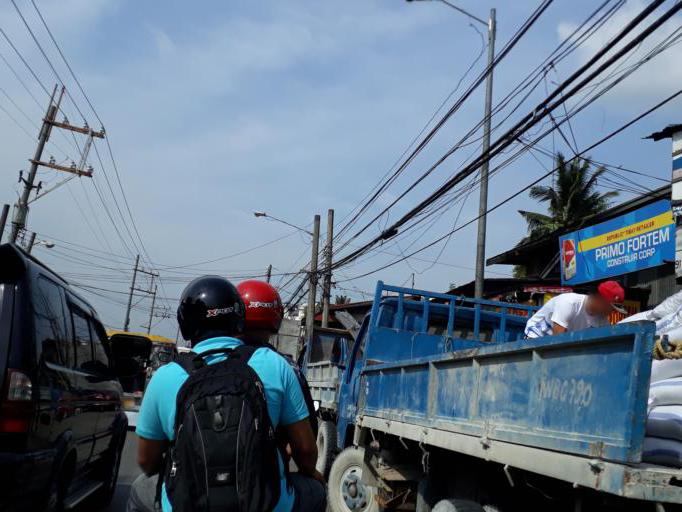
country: PH
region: Calabarzon
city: Bagong Pagasa
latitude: 14.6753
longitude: 121.0148
